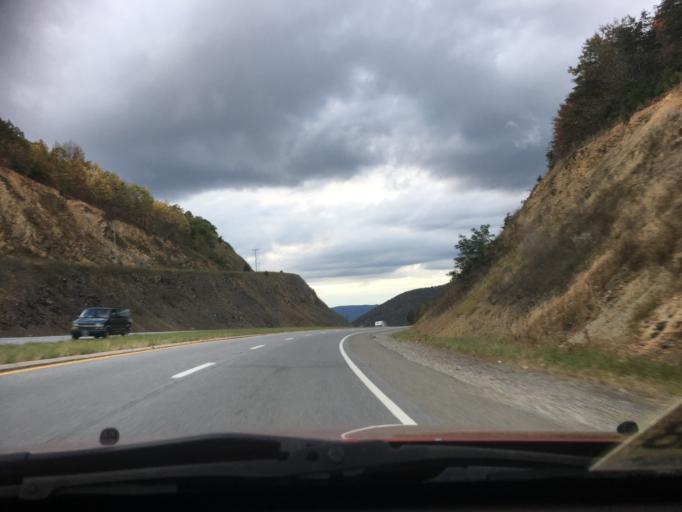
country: US
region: Virginia
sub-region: Pulaski County
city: Dublin
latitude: 37.1797
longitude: -80.7192
